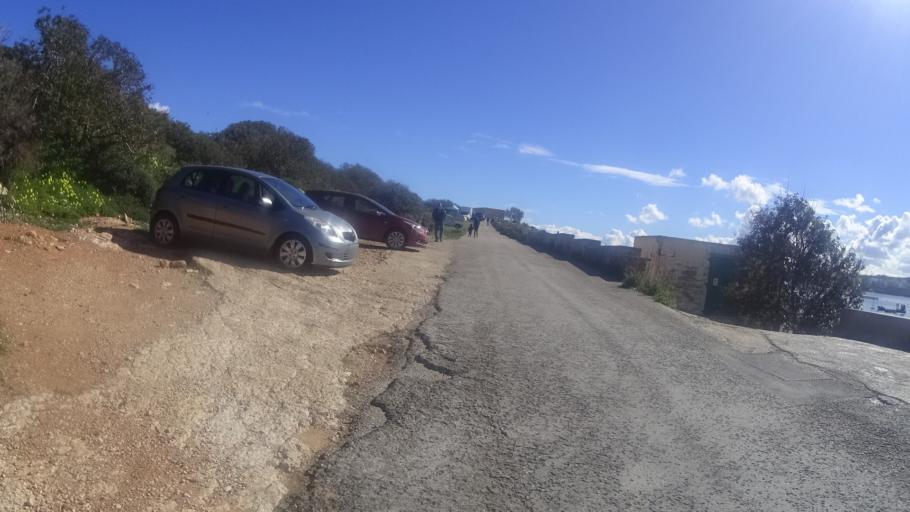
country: MT
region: Saint Paul's Bay
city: San Pawl il-Bahar
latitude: 35.9589
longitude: 14.3927
